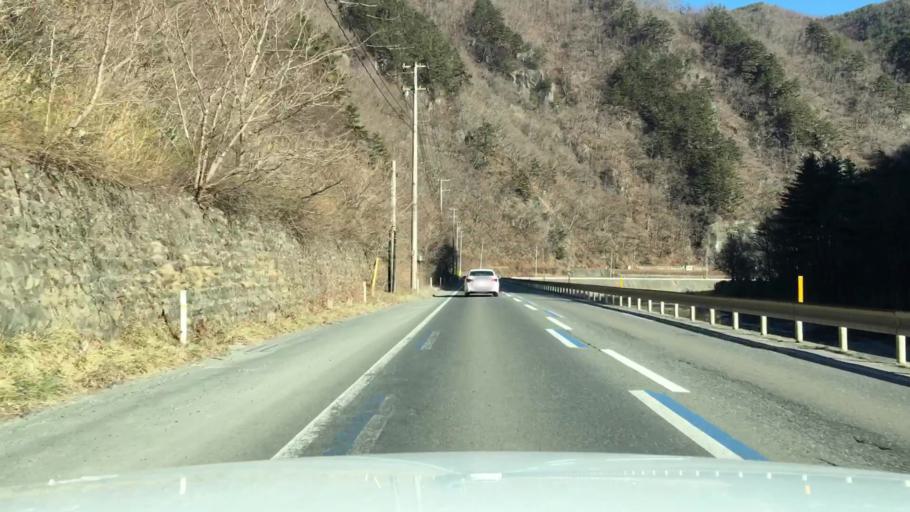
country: JP
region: Iwate
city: Miyako
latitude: 39.6075
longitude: 141.7724
